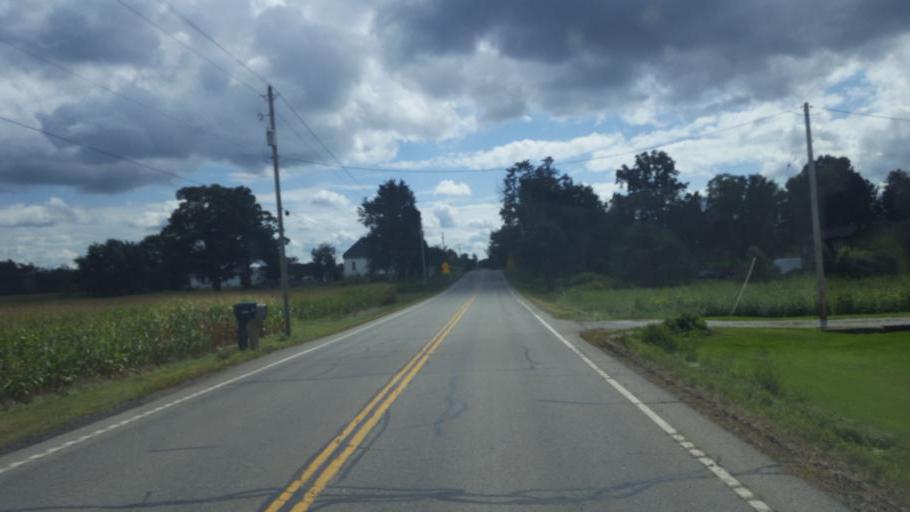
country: US
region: Ohio
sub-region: Richland County
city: Lincoln Heights
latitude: 40.8519
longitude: -82.5136
